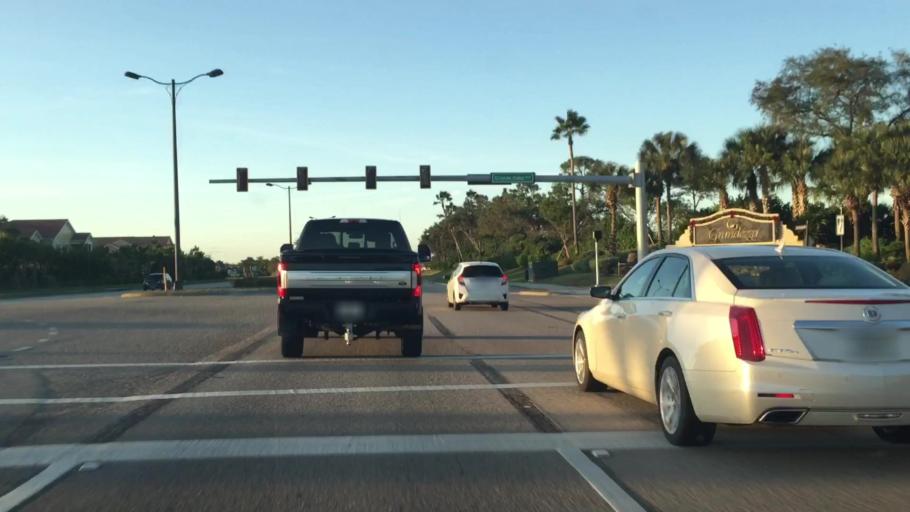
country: US
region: Florida
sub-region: Lee County
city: Estero
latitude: 26.4422
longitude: -81.7723
